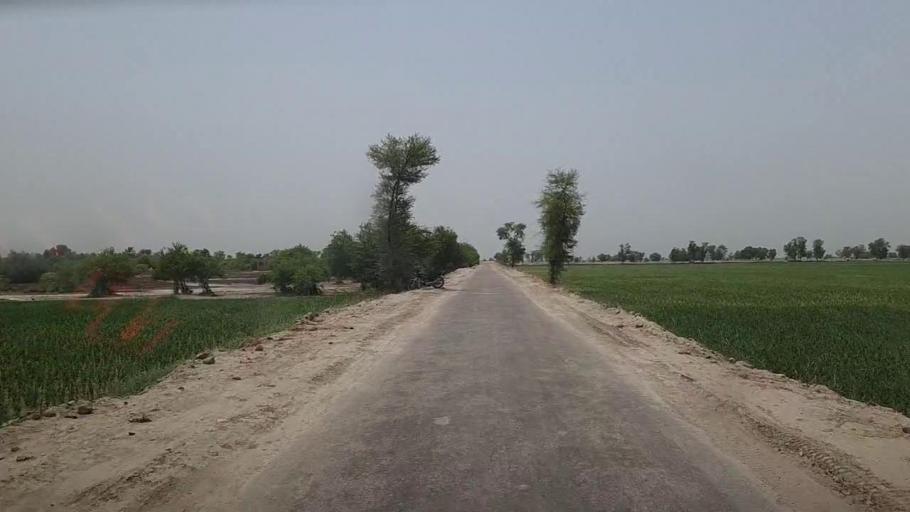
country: PK
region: Sindh
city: Sita Road
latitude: 27.0685
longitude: 67.9052
